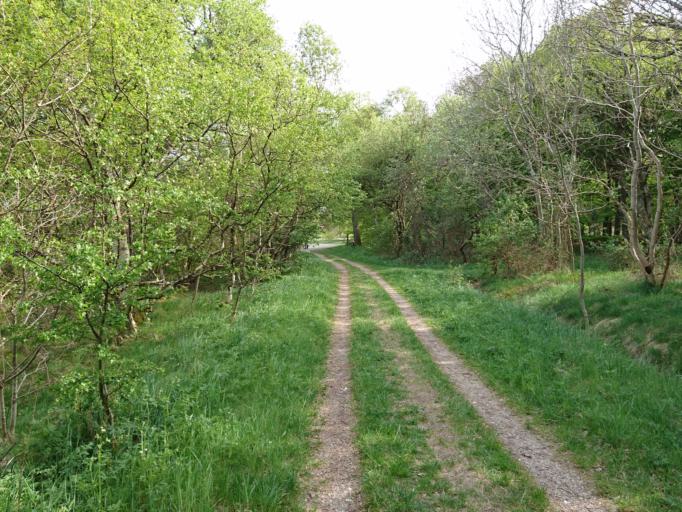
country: DK
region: North Denmark
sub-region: Frederikshavn Kommune
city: Skagen
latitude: 57.7130
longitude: 10.5248
